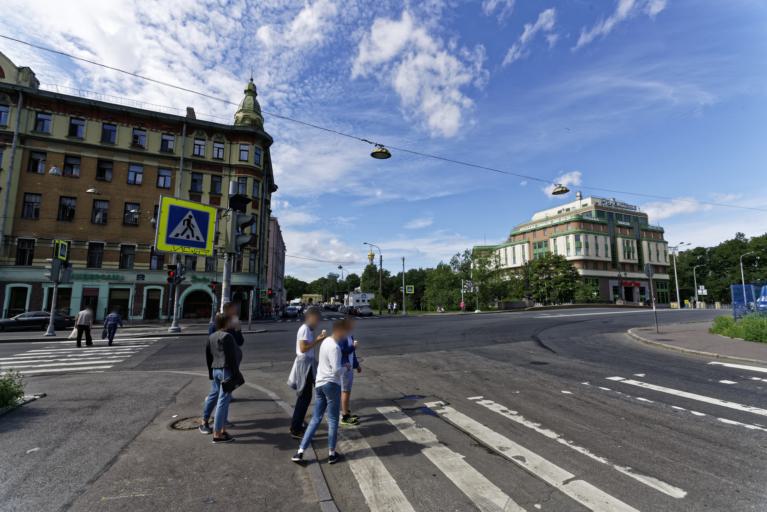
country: RU
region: St.-Petersburg
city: Vasyl'evsky Ostrov
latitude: 59.9469
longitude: 30.2574
